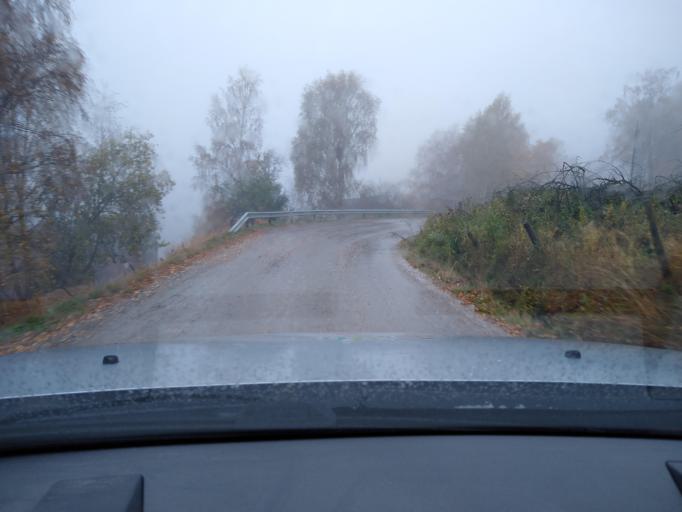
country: NO
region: Oppland
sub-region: Ringebu
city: Ringebu
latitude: 61.5294
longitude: 10.1549
